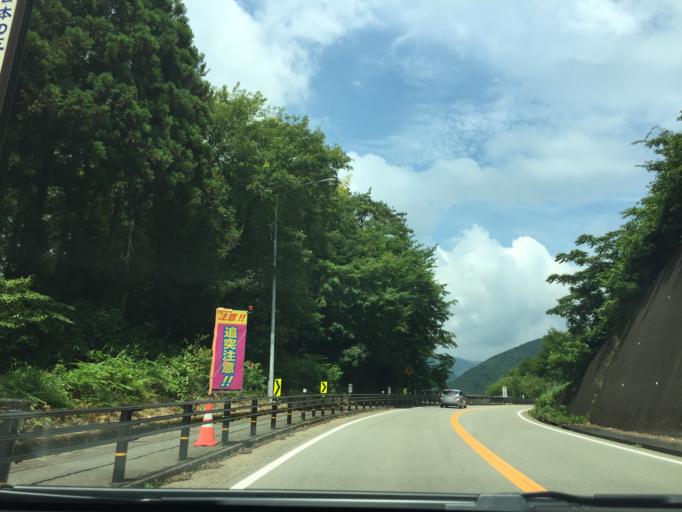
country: JP
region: Gifu
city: Gujo
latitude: 35.8025
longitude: 137.2512
